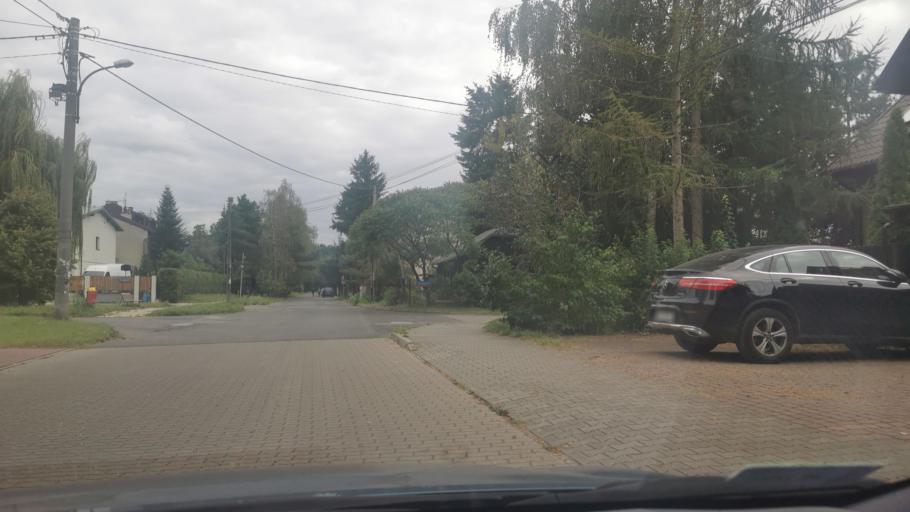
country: PL
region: Masovian Voivodeship
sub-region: Warszawa
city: Wawer
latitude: 52.2106
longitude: 21.1508
